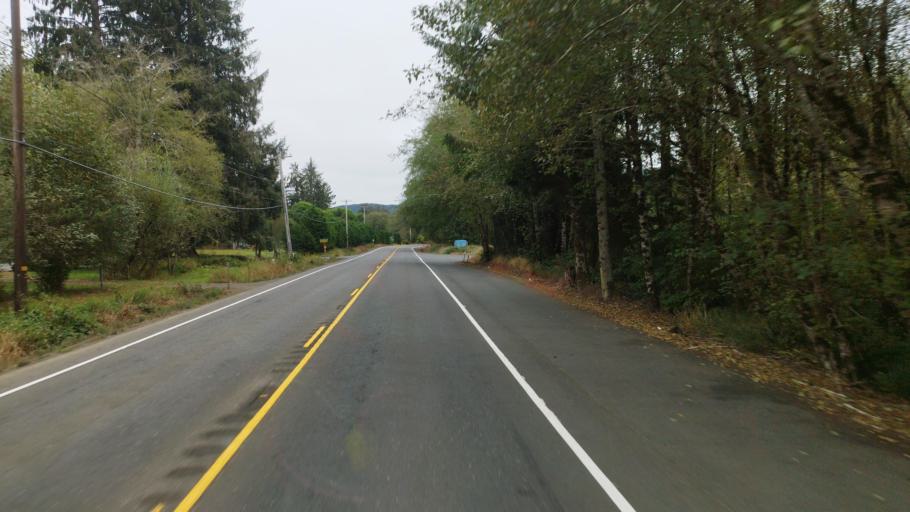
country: US
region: Oregon
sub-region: Clatsop County
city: Cannon Beach
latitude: 45.9146
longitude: -123.8891
